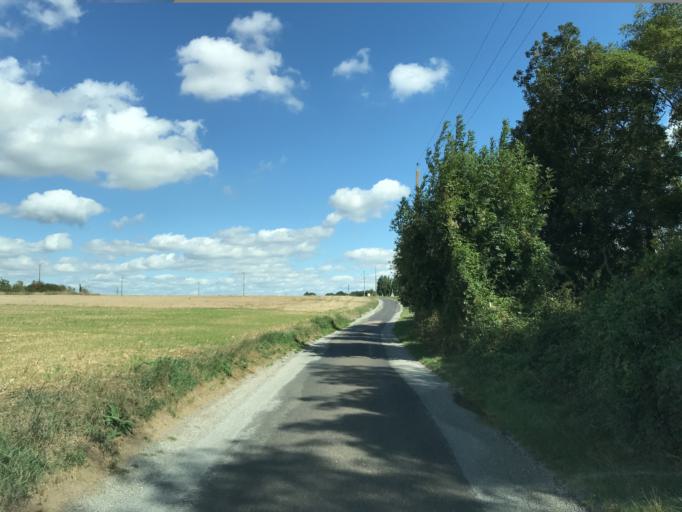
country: FR
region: Haute-Normandie
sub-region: Departement de l'Eure
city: La Chapelle-Reanville
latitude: 49.1254
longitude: 1.3862
